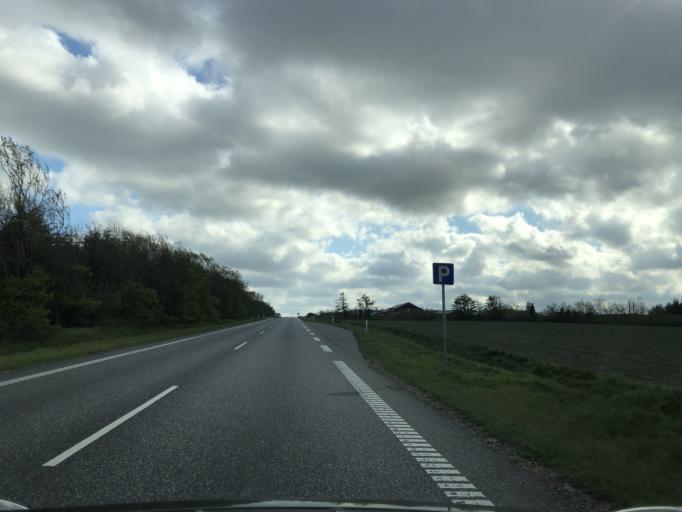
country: DK
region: Central Jutland
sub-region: Ringkobing-Skjern Kommune
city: Videbaek
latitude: 56.2045
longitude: 8.5805
